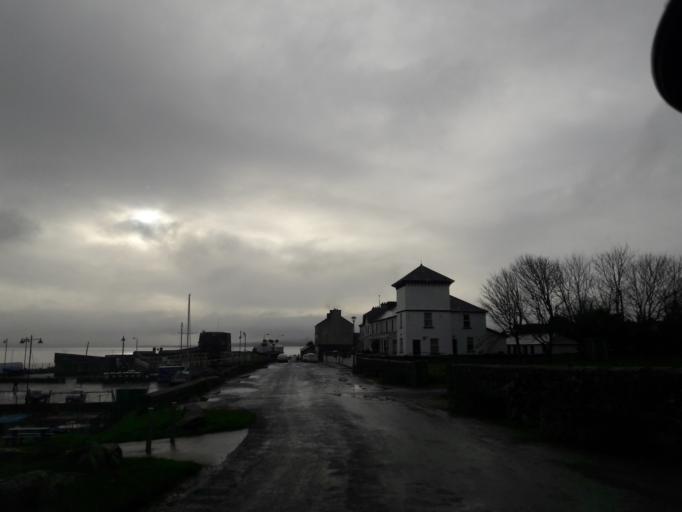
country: IE
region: Ulster
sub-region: County Donegal
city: Buncrana
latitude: 55.0963
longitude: -7.5318
